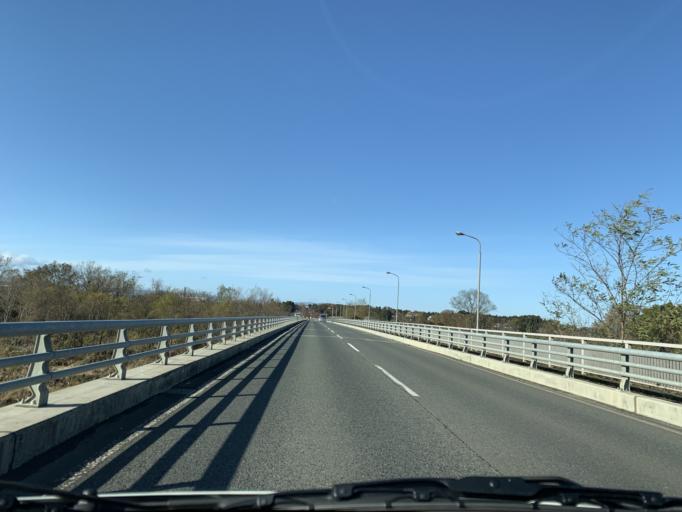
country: JP
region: Iwate
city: Mizusawa
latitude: 39.1863
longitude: 141.1271
